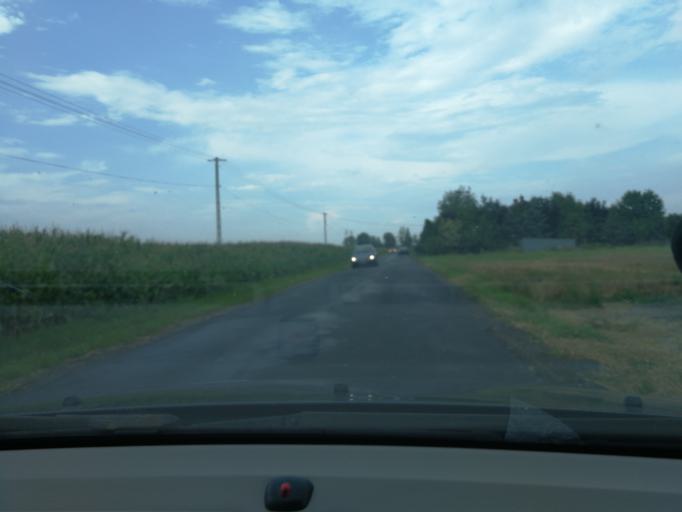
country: PL
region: Masovian Voivodeship
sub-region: Powiat grodziski
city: Grodzisk Mazowiecki
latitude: 52.1279
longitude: 20.5851
